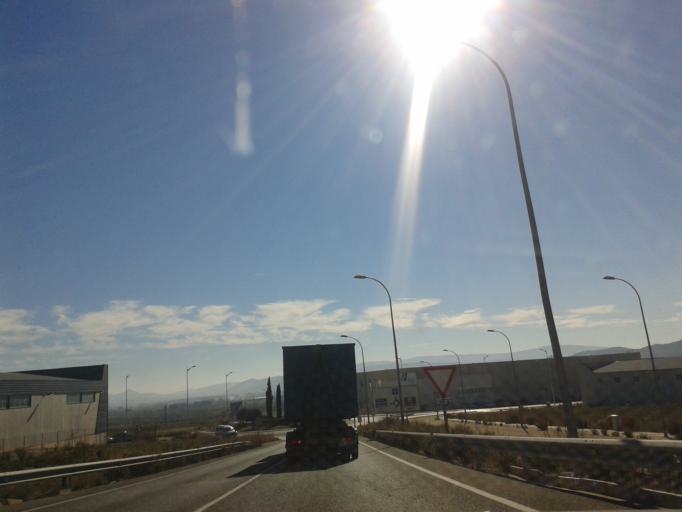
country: ES
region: Castille-La Mancha
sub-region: Provincia de Albacete
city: Caudete
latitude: 38.7149
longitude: -0.9671
